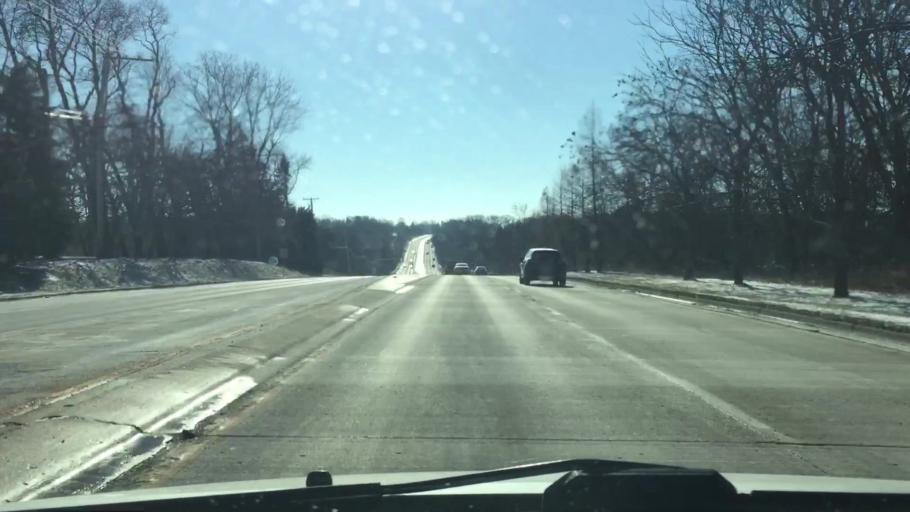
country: US
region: Illinois
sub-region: Kane County
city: West Dundee
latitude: 42.0865
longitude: -88.2897
